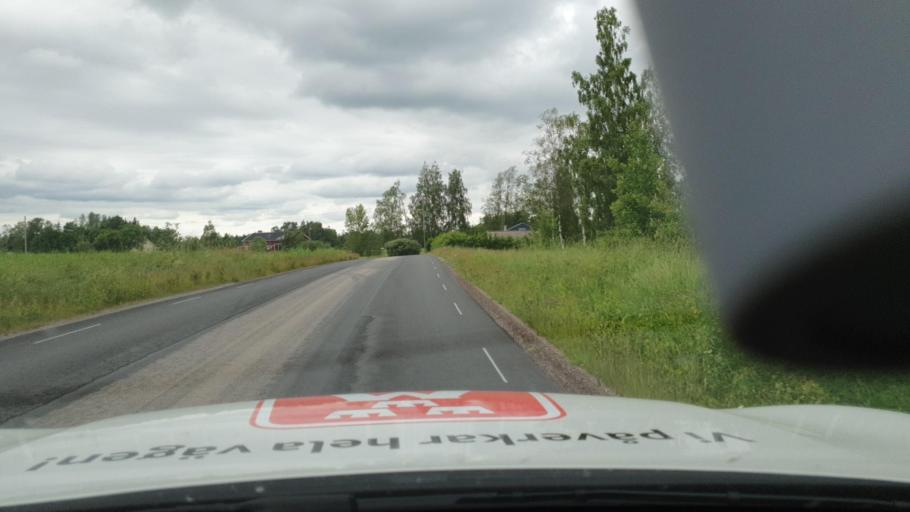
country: SE
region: Vaestra Goetaland
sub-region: Skovde Kommun
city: Skoevde
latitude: 58.3674
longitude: 13.9433
